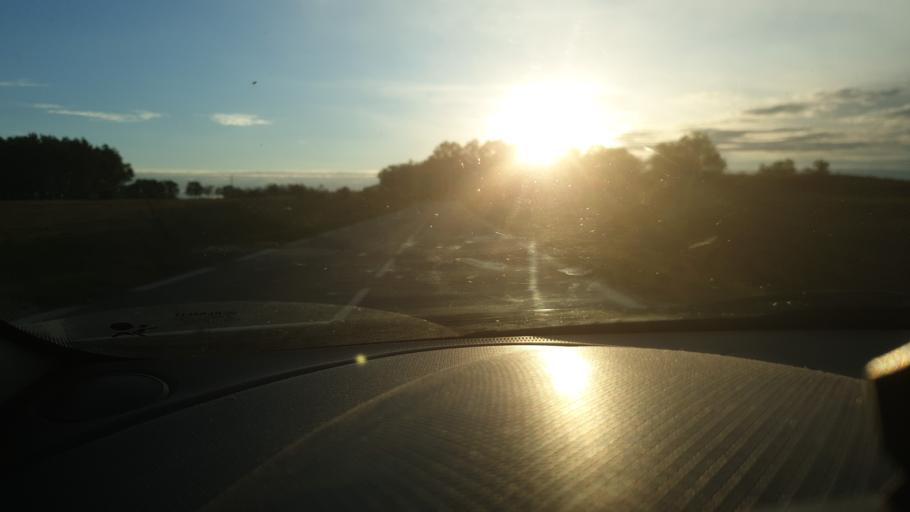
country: FR
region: Midi-Pyrenees
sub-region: Departement du Lot
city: Montcuq
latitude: 44.4020
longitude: 1.2382
